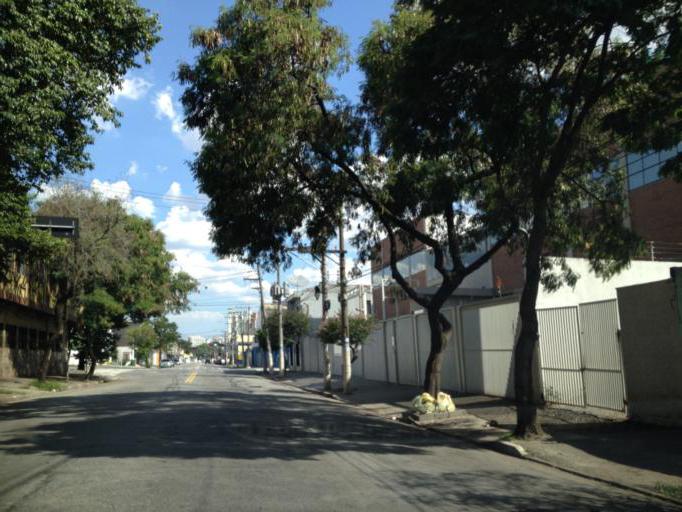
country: BR
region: Sao Paulo
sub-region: Guarulhos
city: Guarulhos
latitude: -23.5122
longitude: -46.5728
